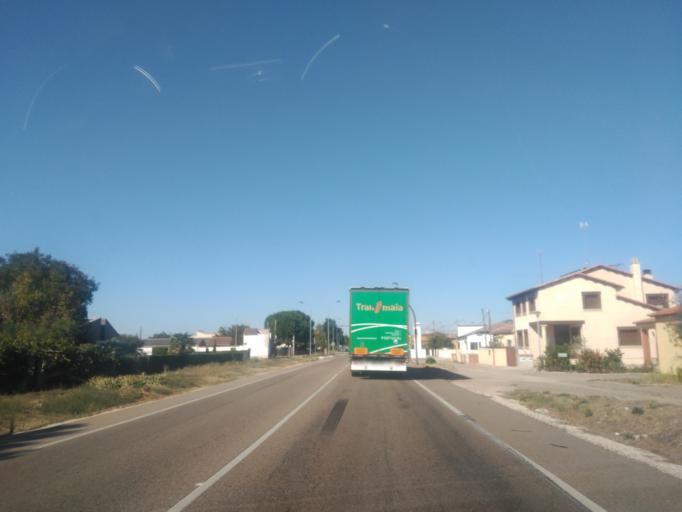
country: ES
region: Castille and Leon
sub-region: Provincia de Valladolid
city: Sardon de Duero
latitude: 41.6075
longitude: -4.4296
